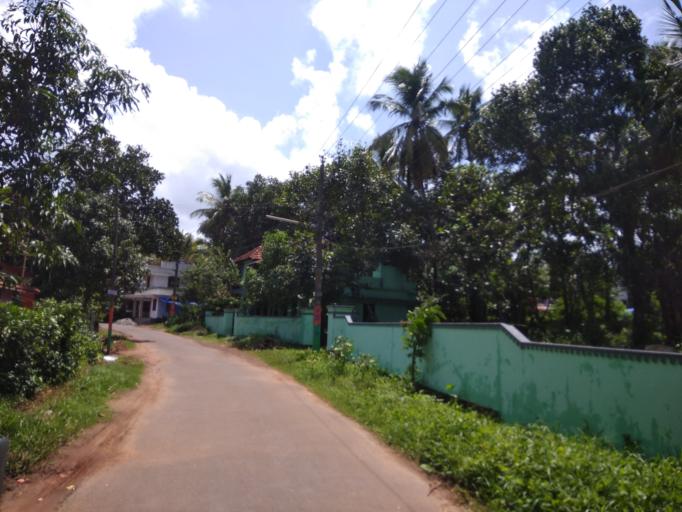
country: IN
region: Kerala
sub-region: Thrissur District
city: Trichur
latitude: 10.5459
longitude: 76.1595
